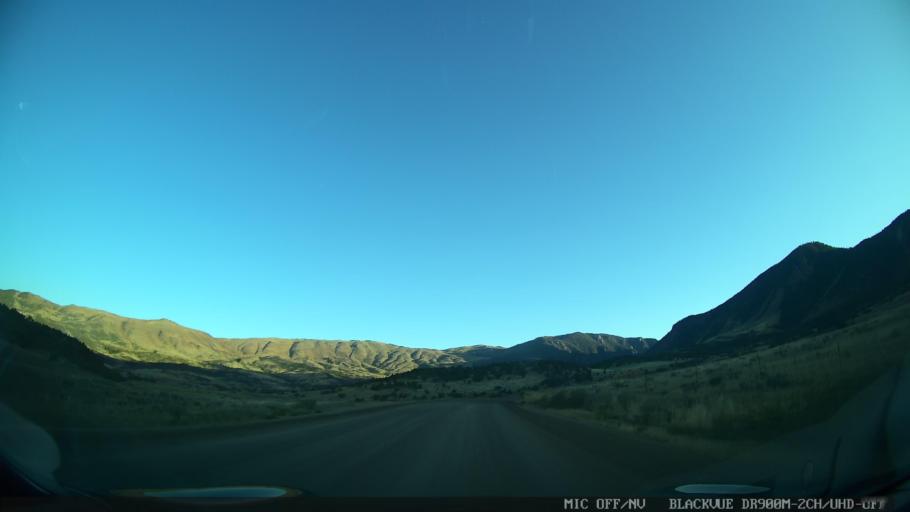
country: US
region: Colorado
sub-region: Grand County
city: Kremmling
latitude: 39.9711
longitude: -106.5022
